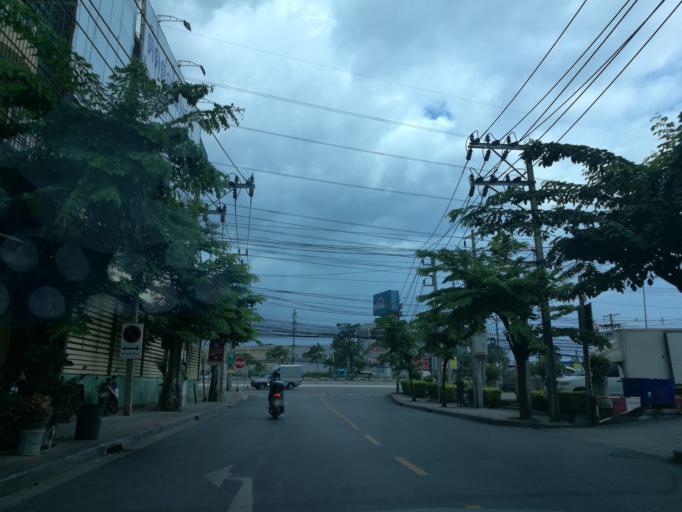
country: TH
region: Bangkok
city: Bang Khun Thian
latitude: 13.6651
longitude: 100.4421
